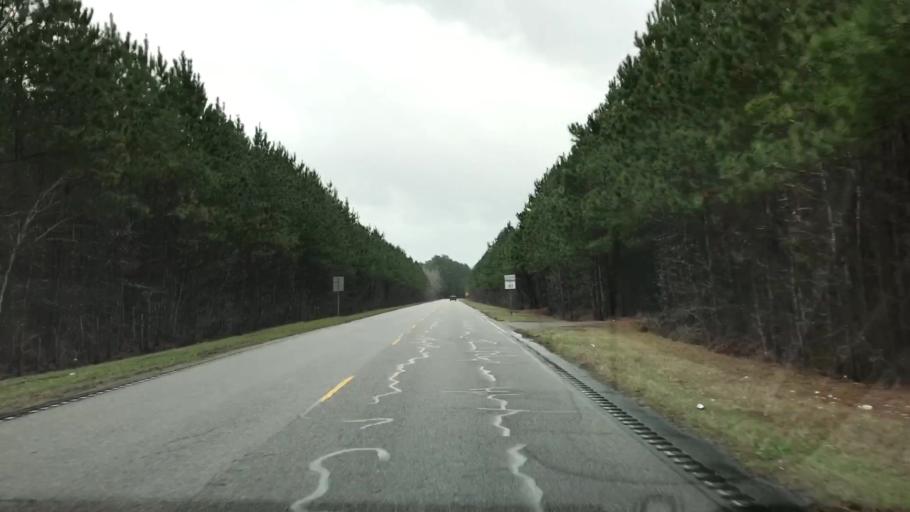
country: US
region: South Carolina
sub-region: Williamsburg County
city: Andrews
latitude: 33.5657
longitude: -79.4531
